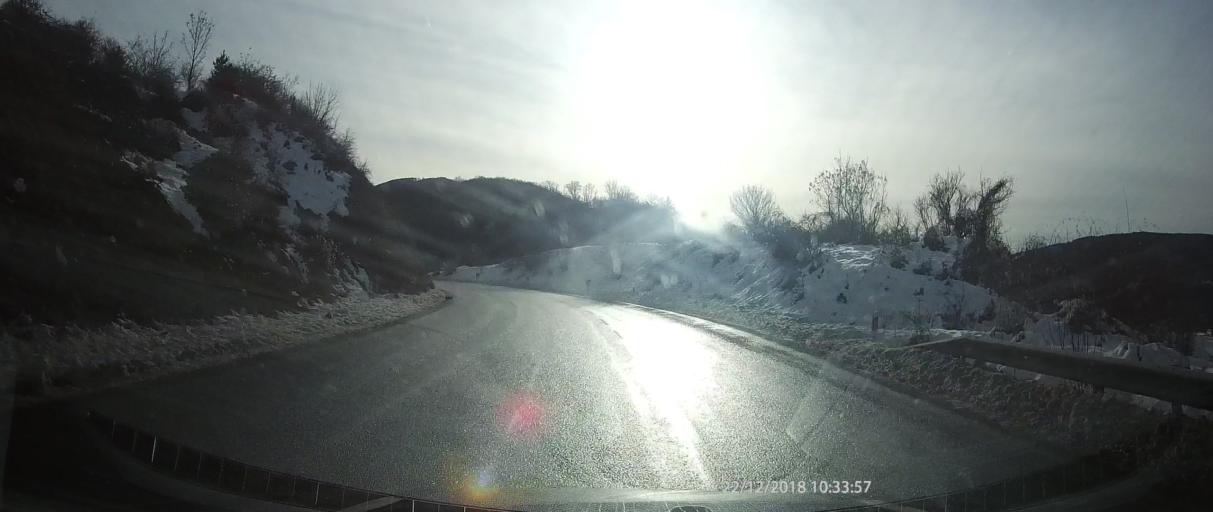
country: MK
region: Kriva Palanka
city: Kriva Palanka
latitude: 42.2179
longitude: 22.4449
